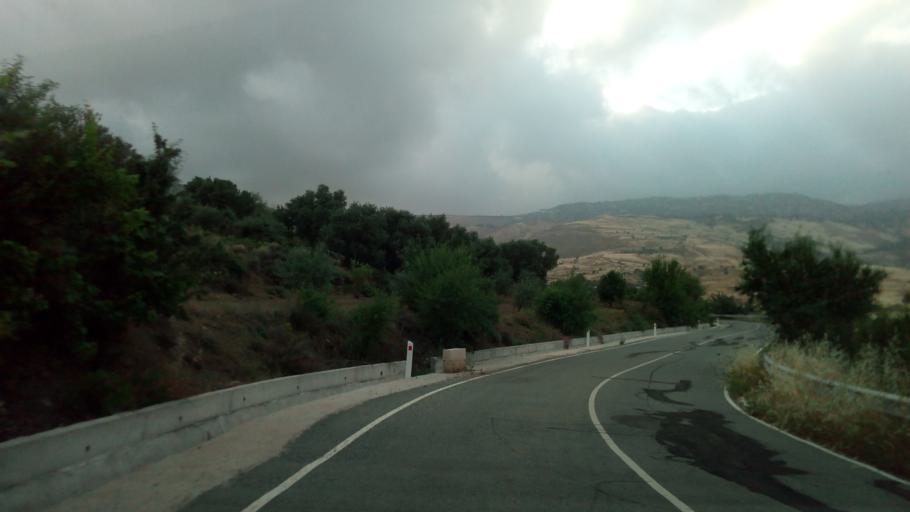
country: CY
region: Limassol
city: Pachna
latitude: 34.8639
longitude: 32.6447
